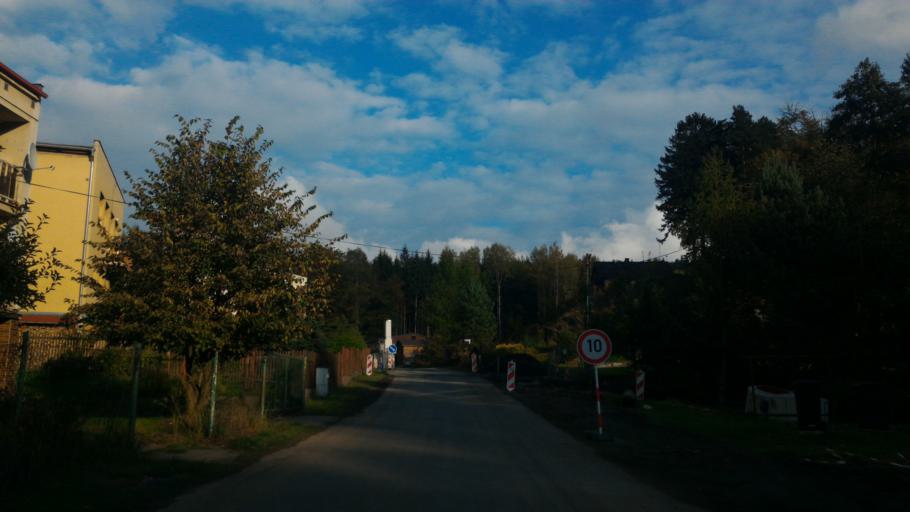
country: CZ
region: Ustecky
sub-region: Okres Decin
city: Chribska
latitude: 50.8561
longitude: 14.5212
